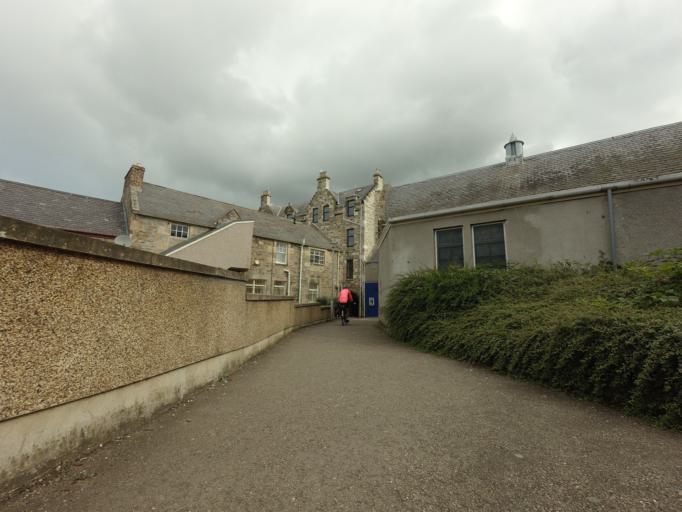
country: GB
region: Scotland
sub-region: Moray
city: Elgin
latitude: 57.6474
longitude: -3.3142
